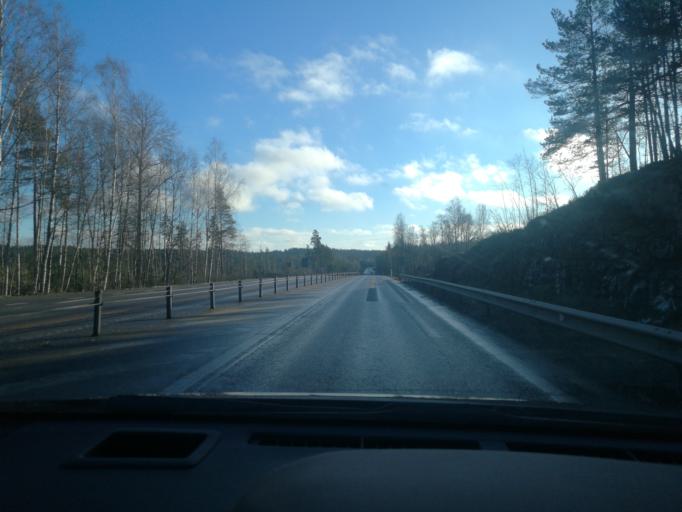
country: SE
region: OEstergoetland
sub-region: Norrkopings Kommun
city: Jursla
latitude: 58.7618
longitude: 16.1726
